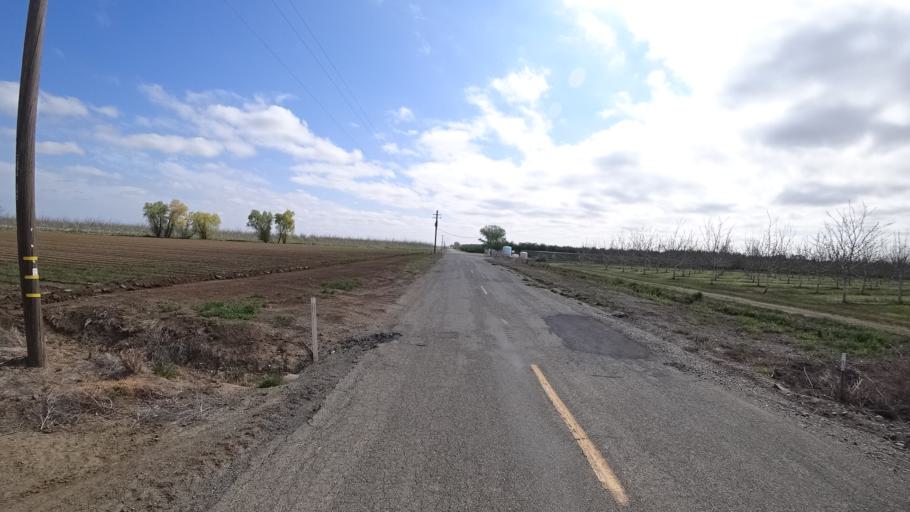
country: US
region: California
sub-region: Colusa County
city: Colusa
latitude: 39.4201
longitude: -121.9487
